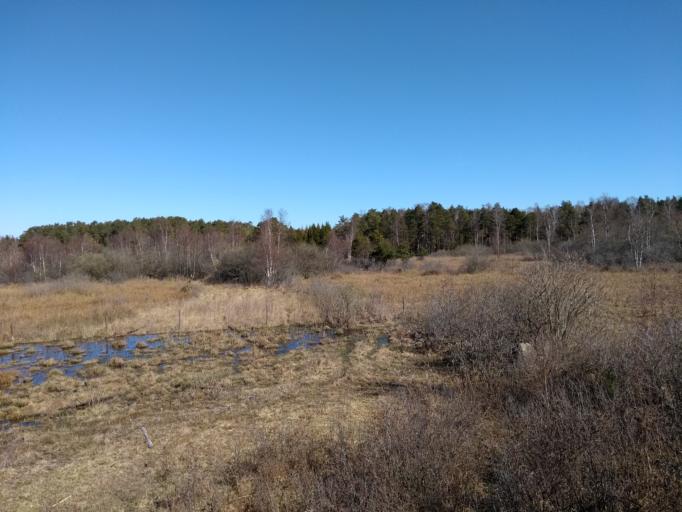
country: SE
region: Kalmar
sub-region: Borgholms Kommun
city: Borgholm
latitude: 56.8618
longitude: 16.7681
